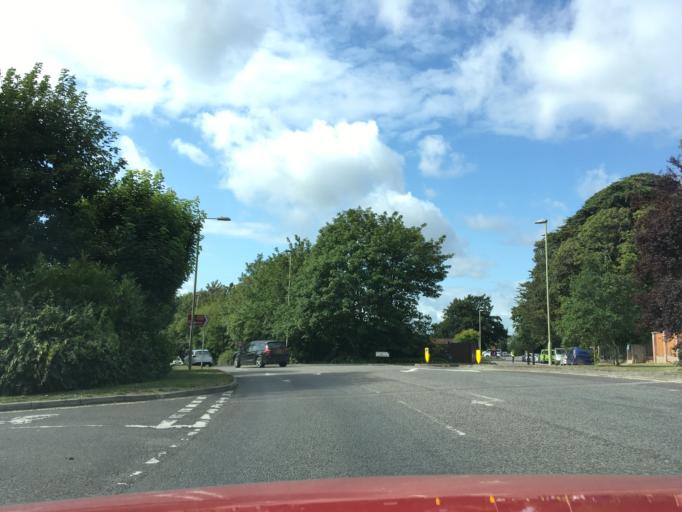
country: GB
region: England
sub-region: Hampshire
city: Havant
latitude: 50.8524
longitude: -1.0097
